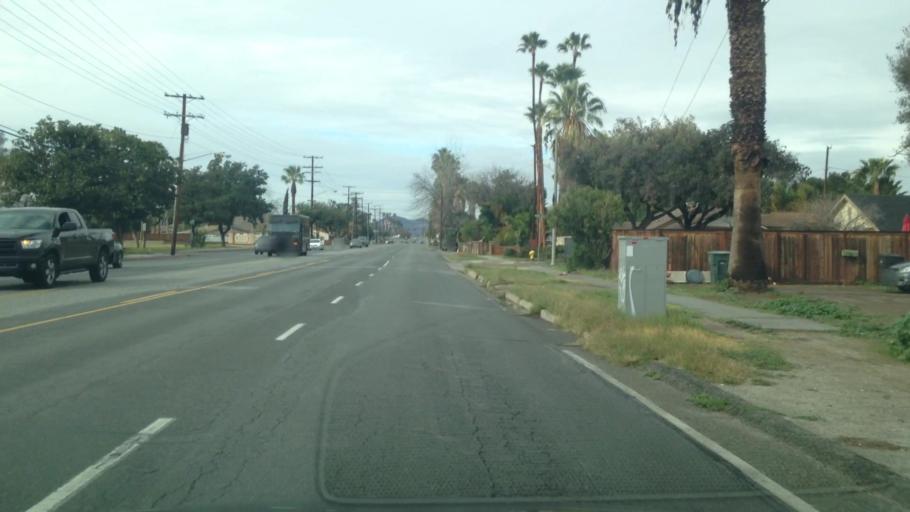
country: US
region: California
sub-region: Riverside County
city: Riverside
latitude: 33.9460
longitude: -117.4272
